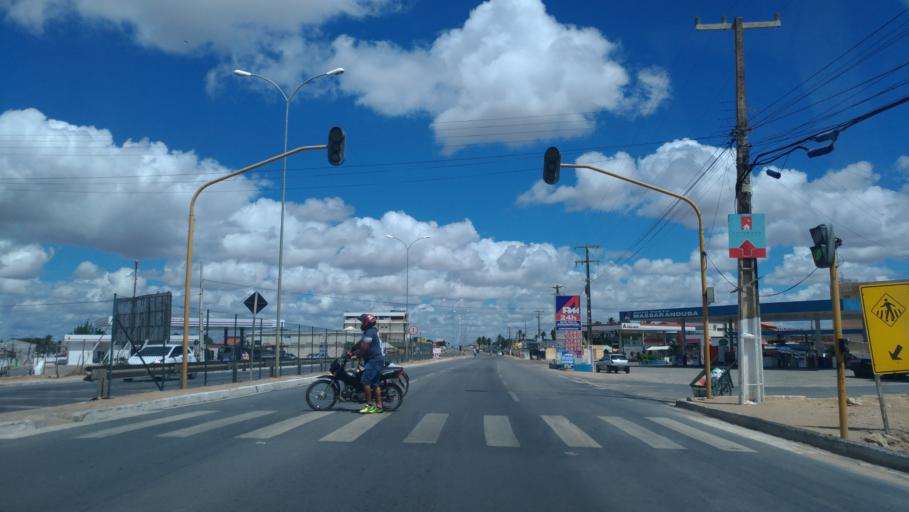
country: BR
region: Alagoas
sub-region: Arapiraca
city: Arapiraca
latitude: -9.7276
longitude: -36.6689
